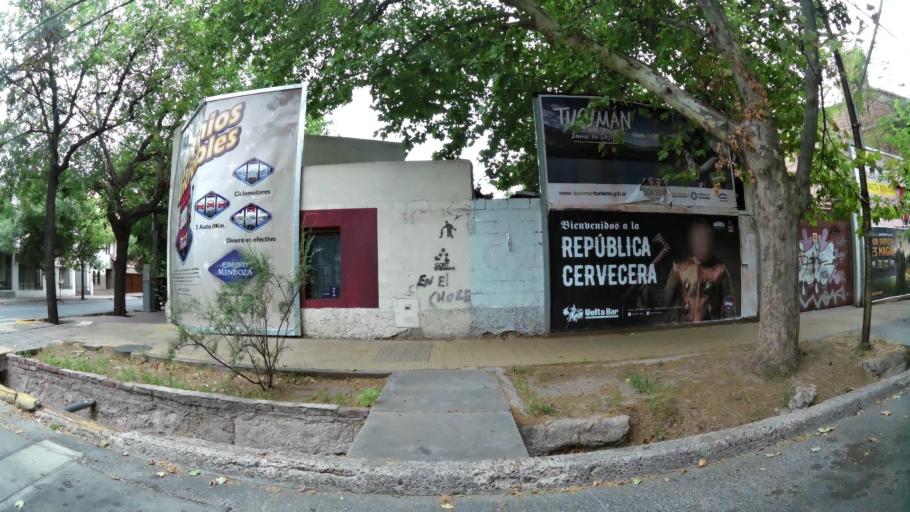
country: AR
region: Mendoza
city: Mendoza
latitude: -32.8925
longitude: -68.8625
